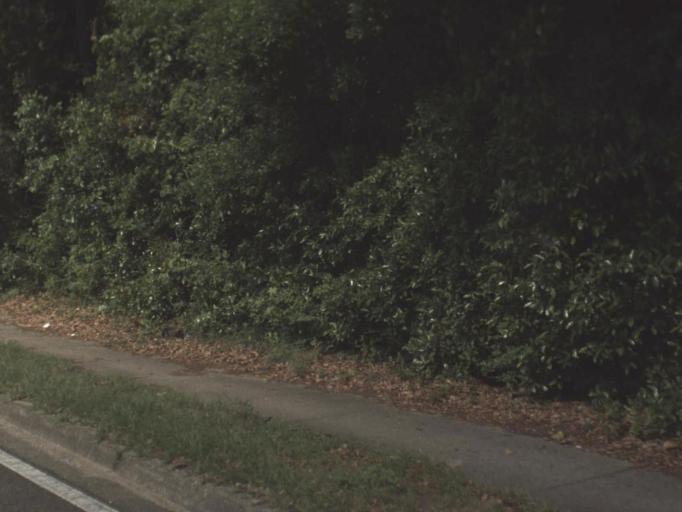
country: US
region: Florida
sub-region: Escambia County
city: Ferry Pass
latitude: 30.5232
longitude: -87.2119
